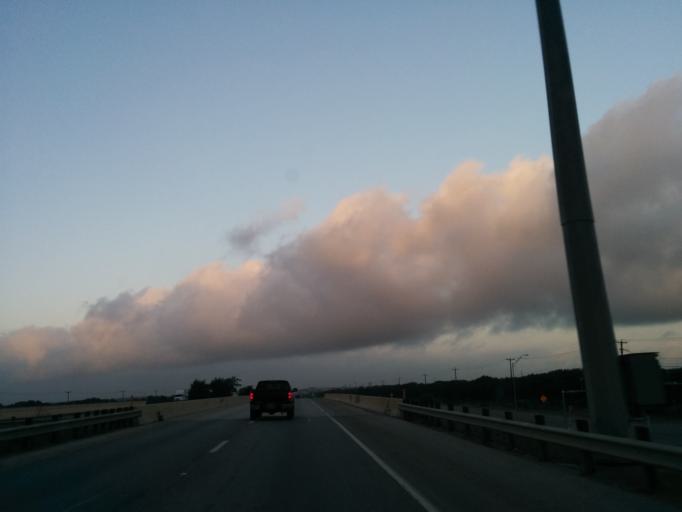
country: US
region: Texas
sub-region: Bexar County
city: Helotes
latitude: 29.5781
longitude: -98.6446
